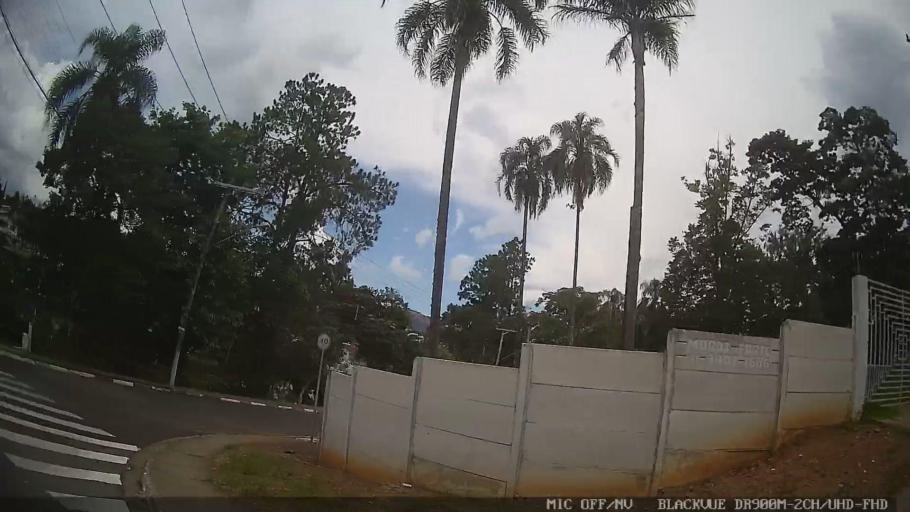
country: BR
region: Sao Paulo
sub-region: Atibaia
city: Atibaia
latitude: -23.1391
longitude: -46.5584
